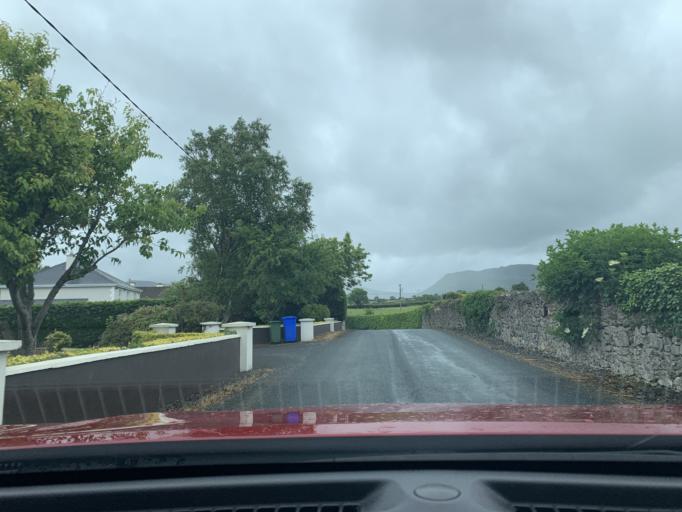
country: IE
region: Connaught
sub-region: Sligo
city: Sligo
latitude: 54.2950
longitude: -8.4624
